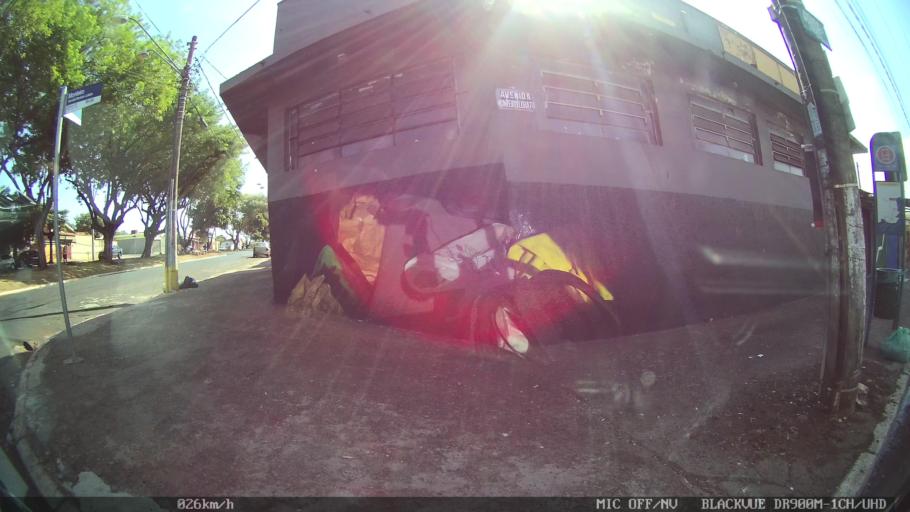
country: BR
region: Sao Paulo
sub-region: Ribeirao Preto
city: Ribeirao Preto
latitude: -21.1869
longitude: -47.8351
